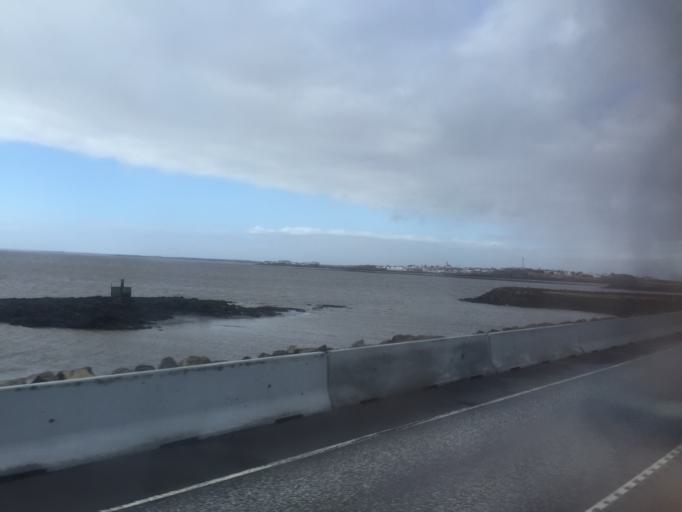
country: IS
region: West
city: Borgarnes
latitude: 64.5303
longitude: -21.8855
